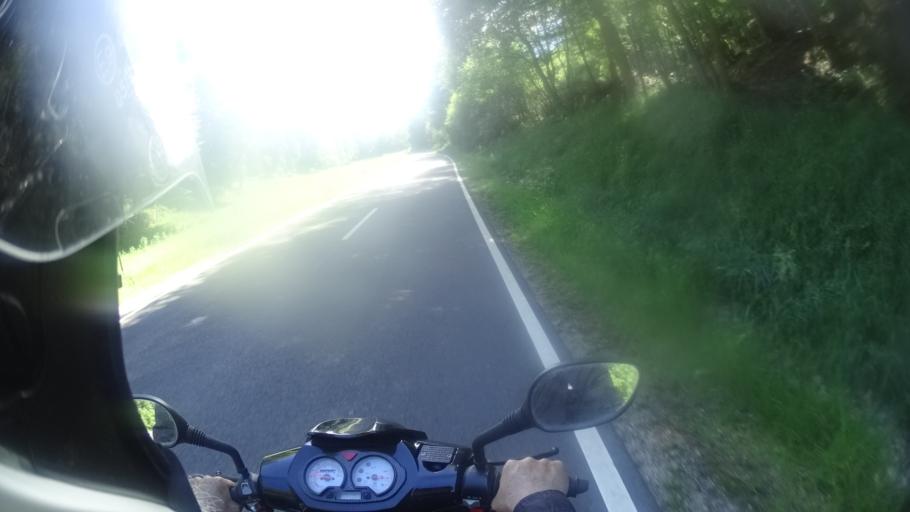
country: DE
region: Hesse
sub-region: Regierungsbezirk Darmstadt
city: Bad Schwalbach
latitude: 50.1015
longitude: 8.0292
